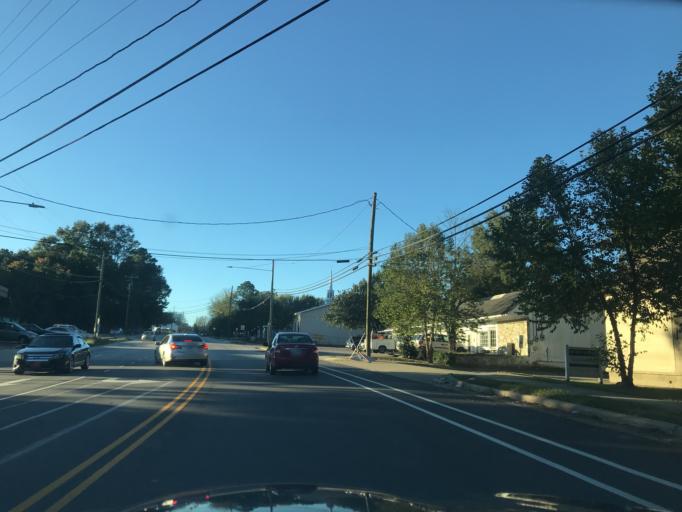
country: US
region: North Carolina
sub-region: Wake County
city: Raleigh
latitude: 35.7688
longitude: -78.6174
